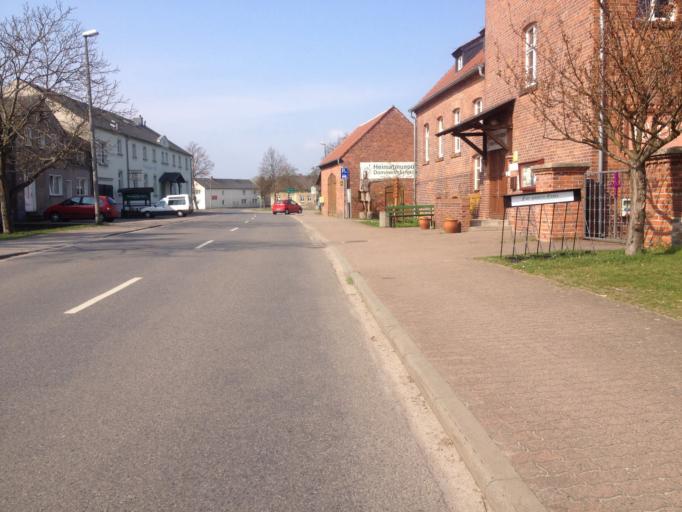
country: DE
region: Brandenburg
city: Briesen
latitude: 51.8264
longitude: 14.2913
